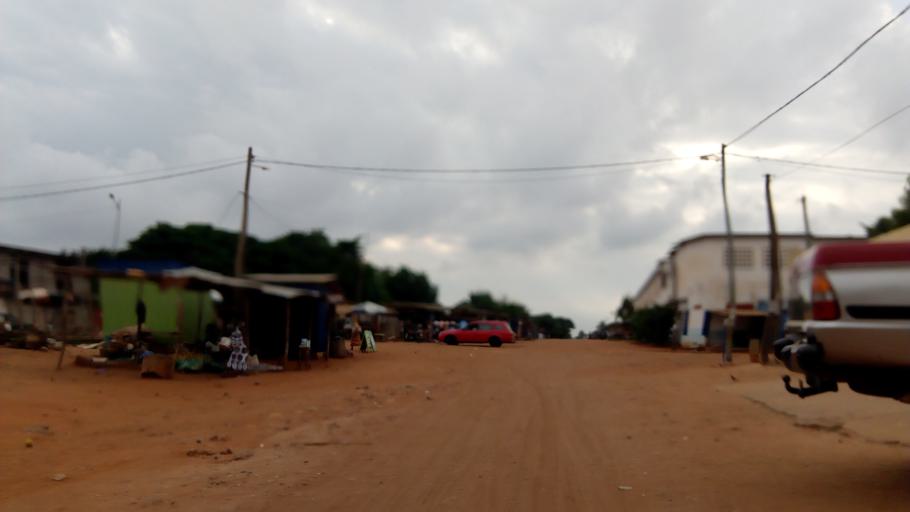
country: TG
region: Maritime
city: Lome
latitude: 6.1758
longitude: 1.1917
